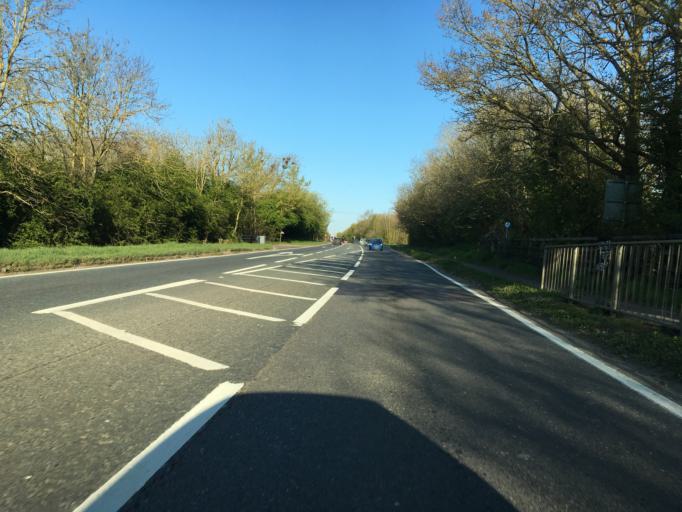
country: GB
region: England
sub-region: Oxfordshire
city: Eynsham
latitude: 51.7903
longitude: -1.4076
